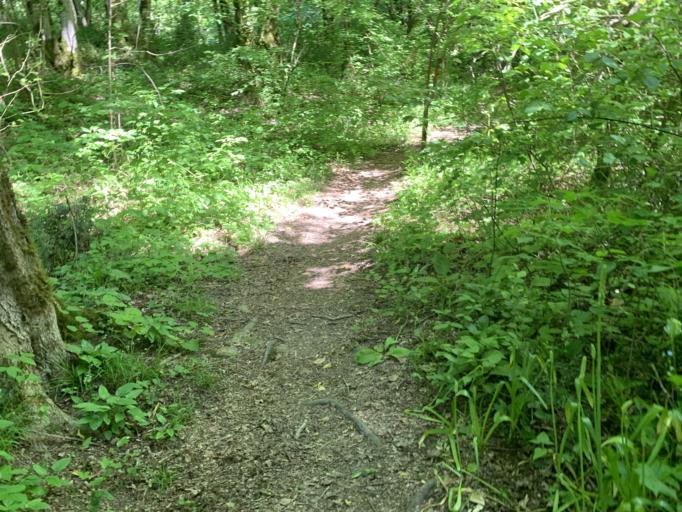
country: RU
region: Krasnodarskiy
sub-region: Sochi City
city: Lazarevskoye
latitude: 43.9478
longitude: 39.3173
